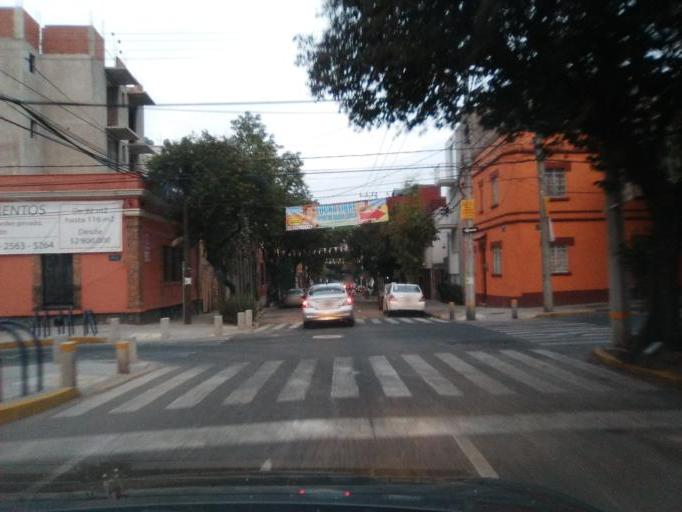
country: MX
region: Mexico City
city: Alvaro Obregon
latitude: 19.3713
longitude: -99.1906
